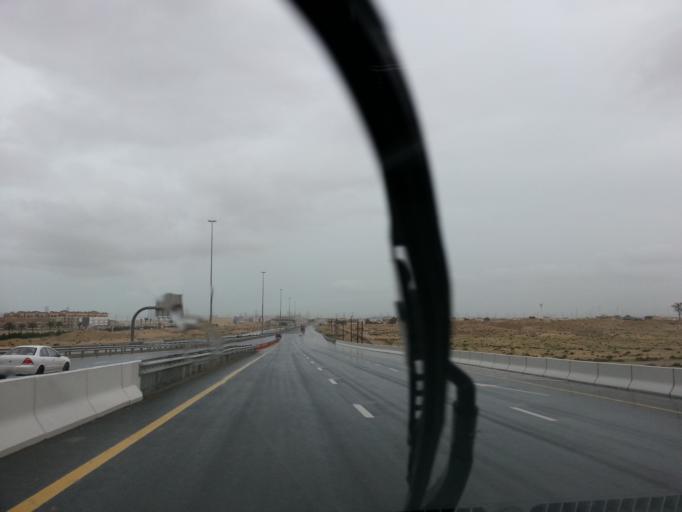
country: AE
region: Dubai
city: Dubai
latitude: 25.0563
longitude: 55.2227
